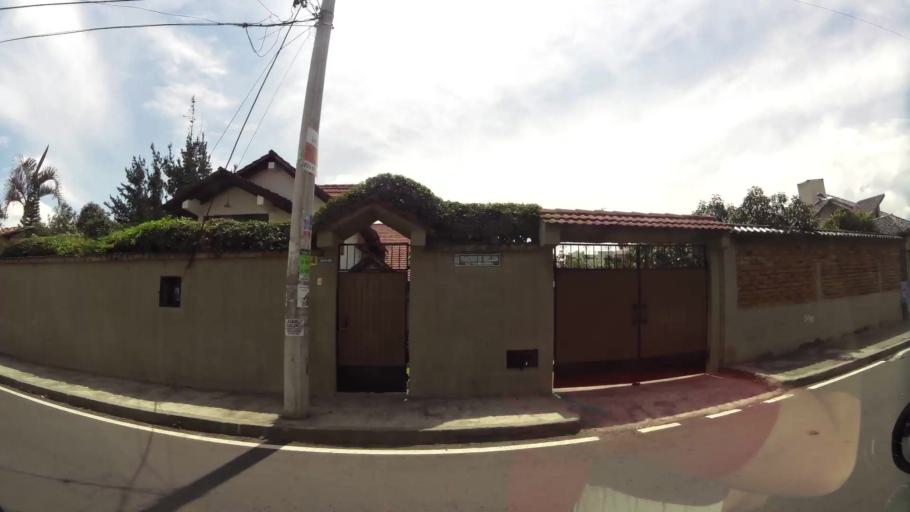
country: EC
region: Pichincha
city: Quito
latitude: -0.2114
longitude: -78.4075
